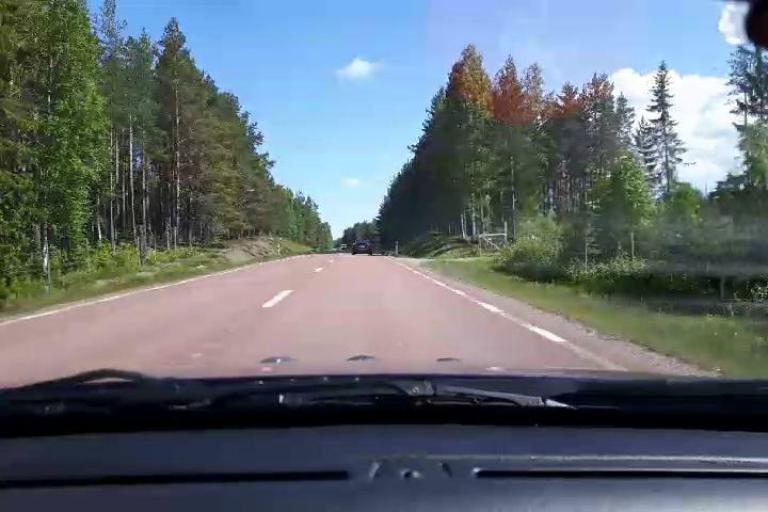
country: SE
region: Gaevleborg
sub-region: Hudiksvalls Kommun
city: Delsbo
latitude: 61.7931
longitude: 16.5831
